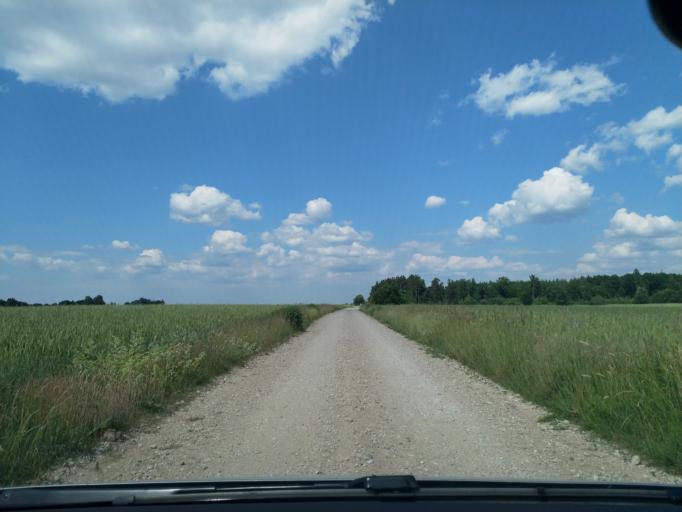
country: LV
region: Kuldigas Rajons
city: Kuldiga
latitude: 56.9649
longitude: 21.9092
